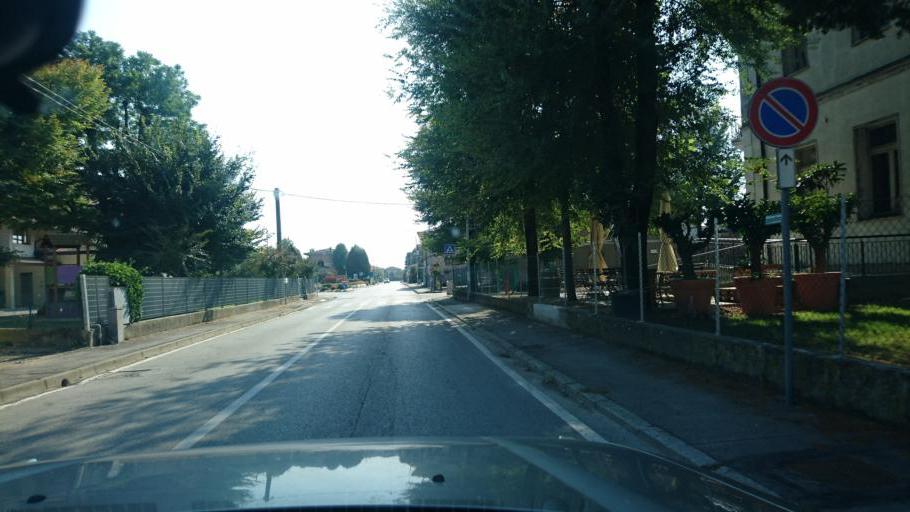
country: IT
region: Veneto
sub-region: Provincia di Padova
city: Campodoro
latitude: 45.5112
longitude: 11.7414
